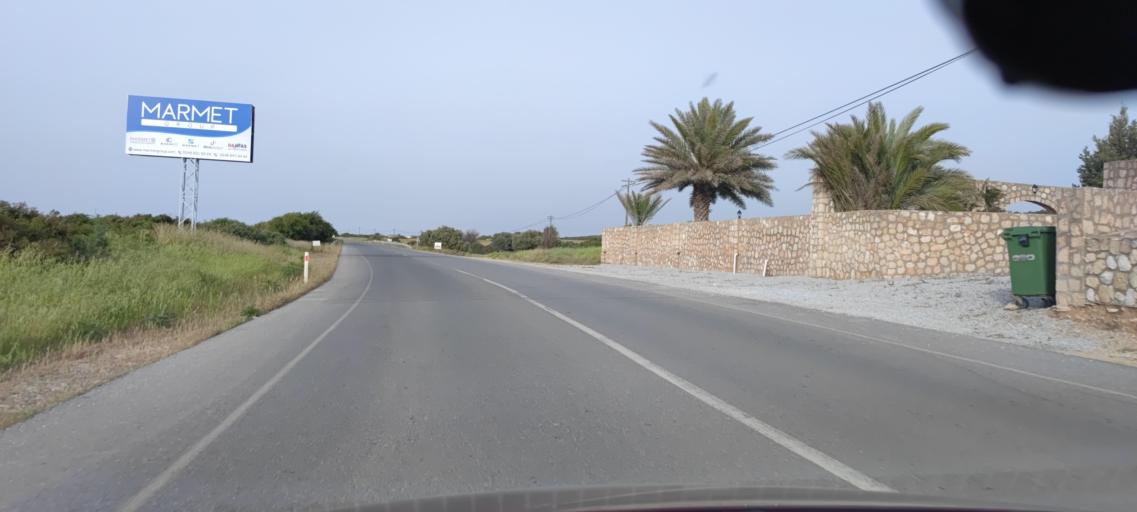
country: CY
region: Ammochostos
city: Leonarisso
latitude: 35.5590
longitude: 34.2393
